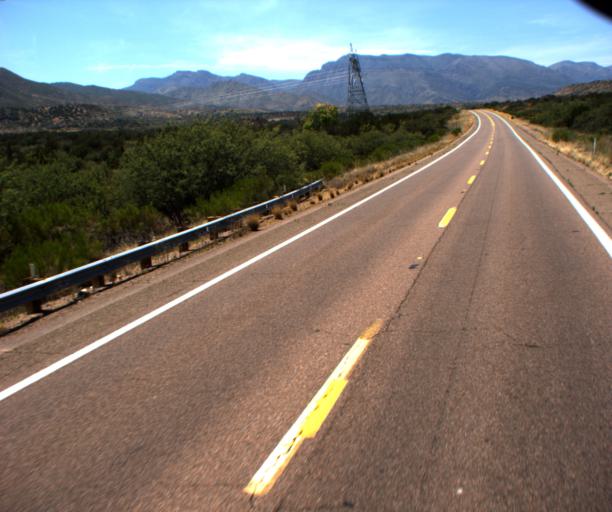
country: US
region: Arizona
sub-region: Gila County
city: Tonto Basin
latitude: 34.0273
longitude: -111.3470
